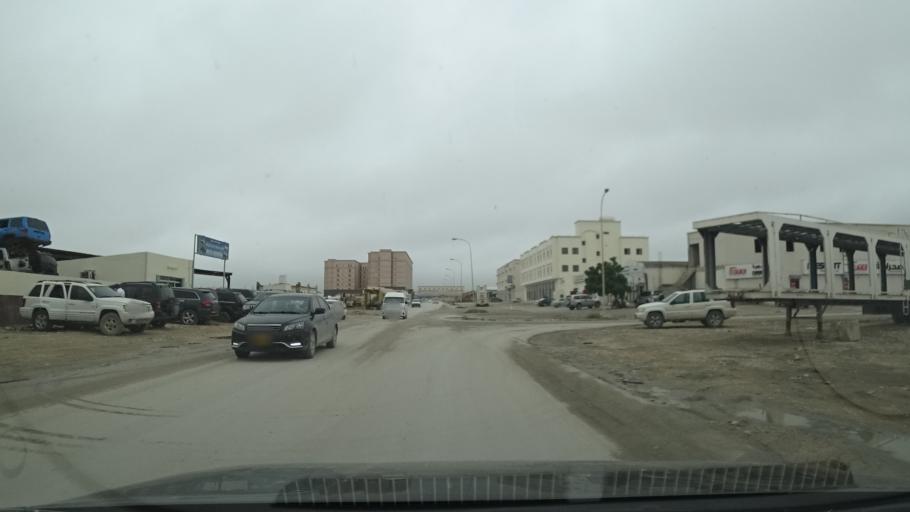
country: OM
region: Zufar
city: Salalah
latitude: 17.0196
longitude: 54.0413
